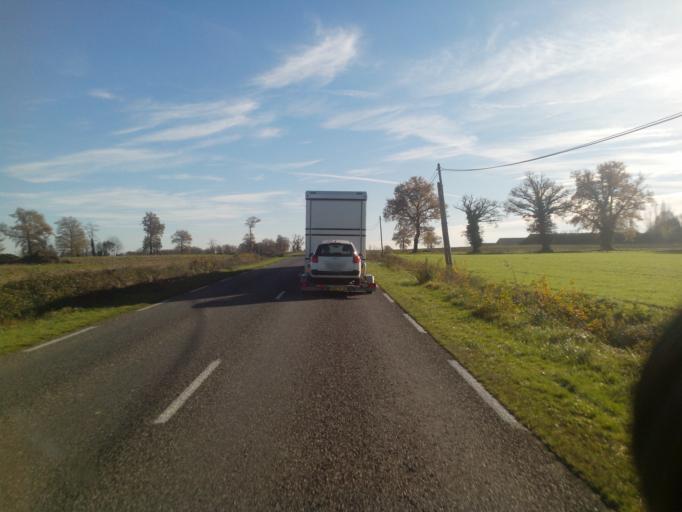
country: FR
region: Limousin
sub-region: Departement de la Haute-Vienne
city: Bellac
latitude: 46.0784
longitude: 1.0936
